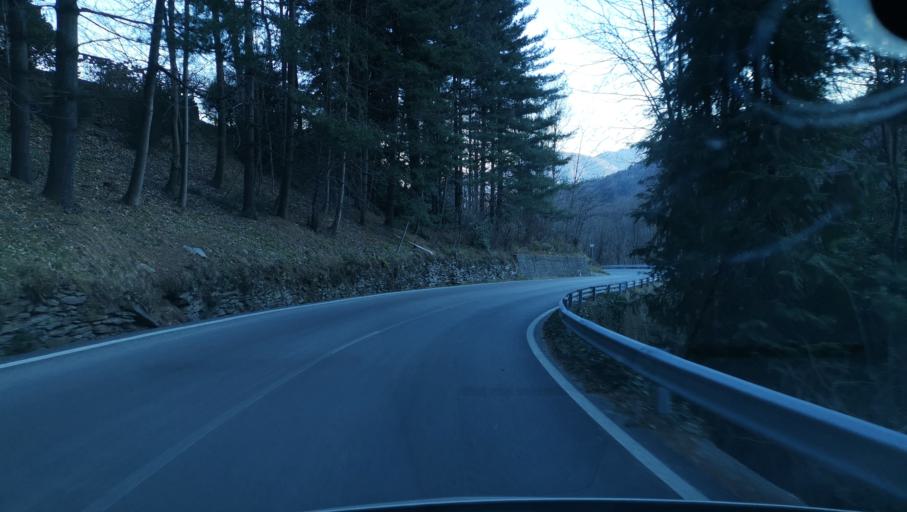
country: IT
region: Piedmont
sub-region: Provincia di Cuneo
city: Bagnolo Piemonte
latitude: 44.7520
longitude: 7.2620
